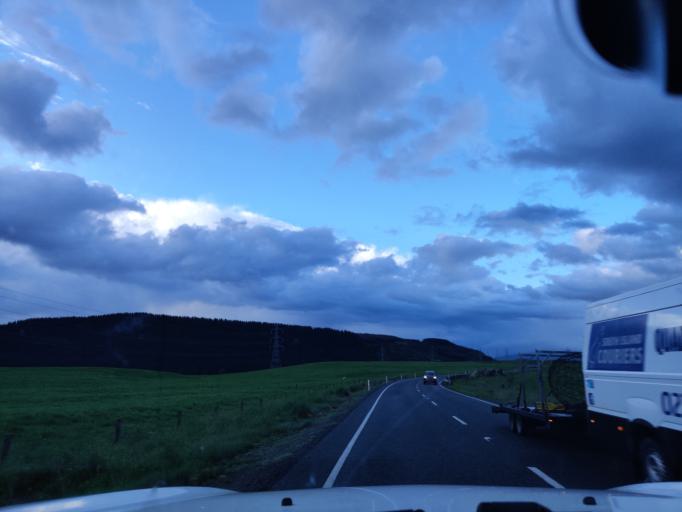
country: NZ
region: Waikato
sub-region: South Waikato District
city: Tokoroa
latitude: -38.3669
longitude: 175.8056
